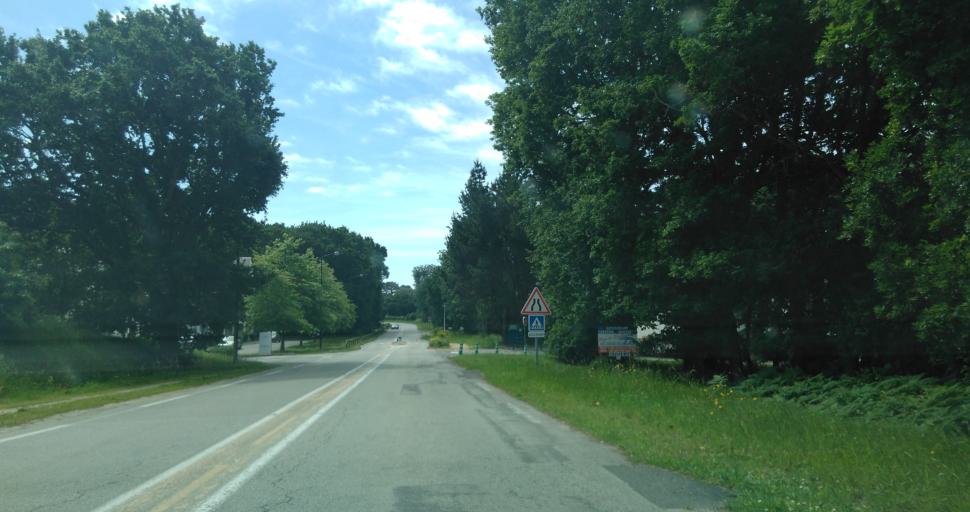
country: FR
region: Brittany
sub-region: Departement du Morbihan
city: La Trinite-sur-Mer
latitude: 47.5934
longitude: -3.0359
